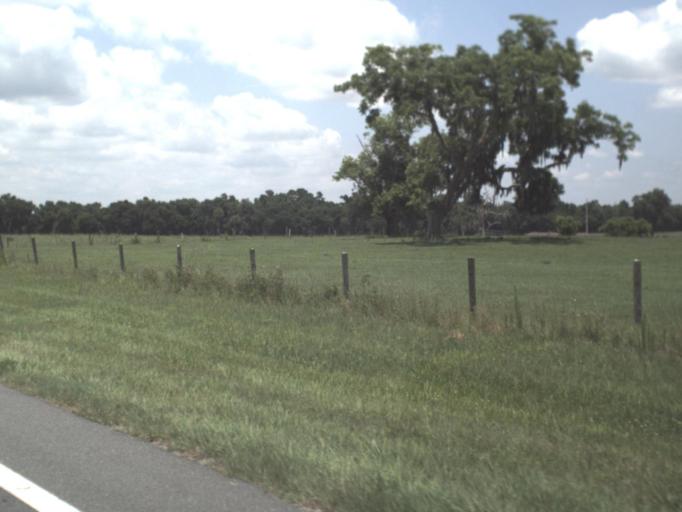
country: US
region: Florida
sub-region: Alachua County
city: Archer
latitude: 29.5099
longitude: -82.4064
